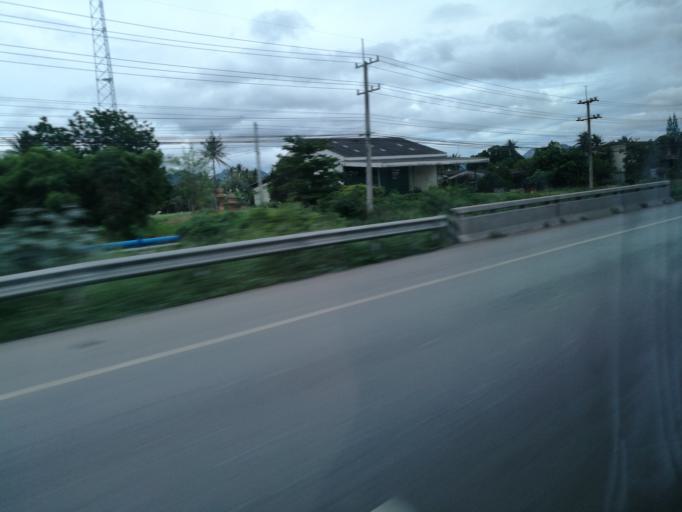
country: TH
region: Prachuap Khiri Khan
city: Sam Roi Yot
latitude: 12.2517
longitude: 99.8707
